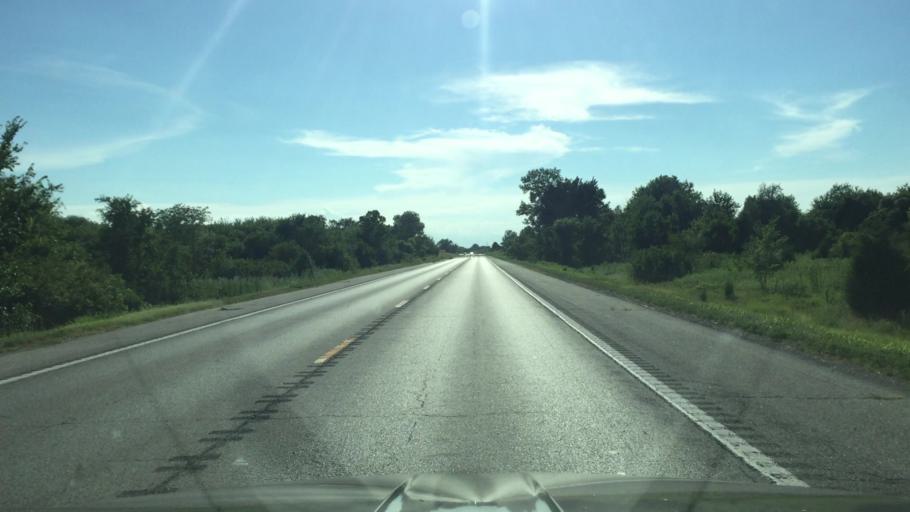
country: US
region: Missouri
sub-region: Pettis County
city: Sedalia
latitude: 38.6949
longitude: -93.1279
